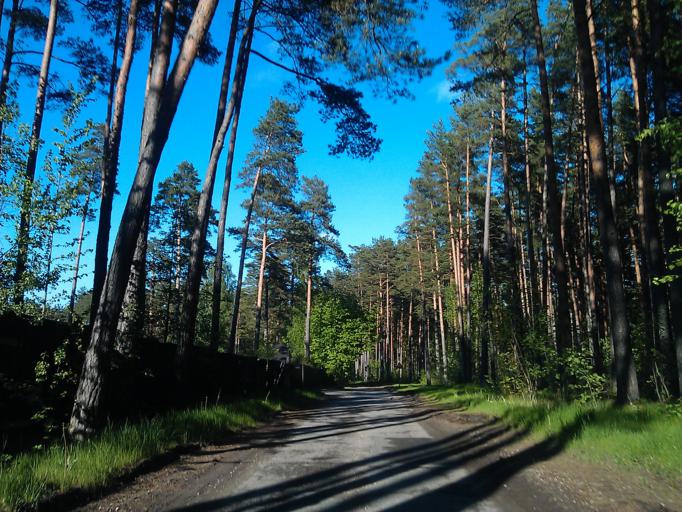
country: LV
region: Riga
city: Bergi
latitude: 57.0129
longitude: 24.2820
